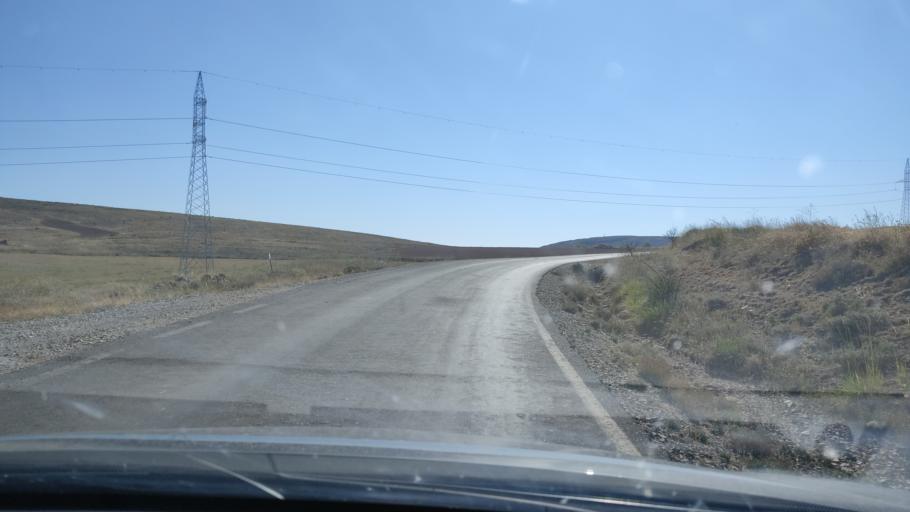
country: ES
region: Aragon
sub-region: Provincia de Teruel
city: Monforte de Moyuela
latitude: 41.0430
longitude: -0.9906
